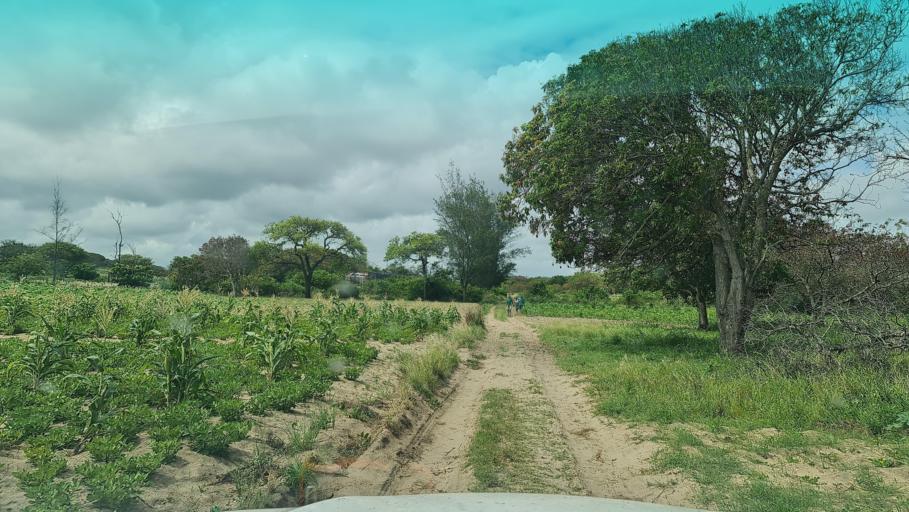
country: MZ
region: Maputo
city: Manhica
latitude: -25.3974
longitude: 33.0278
